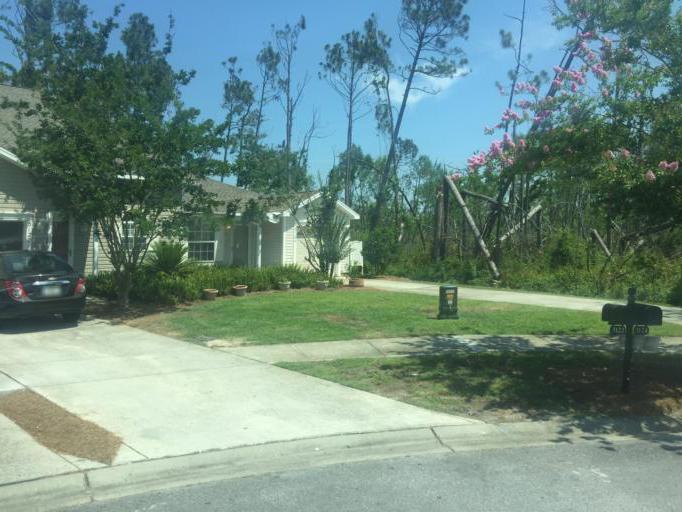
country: US
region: Florida
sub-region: Bay County
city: Hiland Park
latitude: 30.2130
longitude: -85.6364
